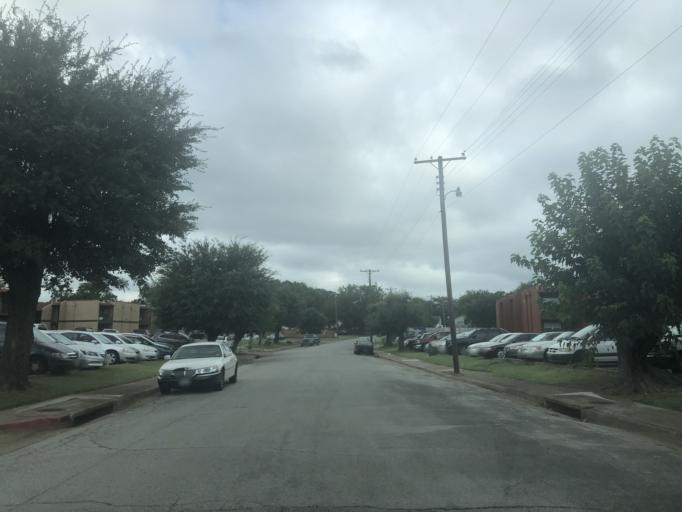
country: US
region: Texas
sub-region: Dallas County
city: Duncanville
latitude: 32.6552
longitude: -96.9065
